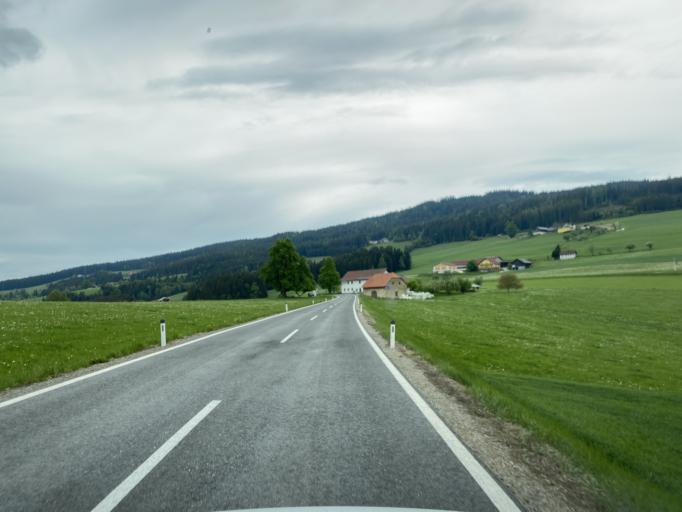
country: AT
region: Styria
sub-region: Politischer Bezirk Weiz
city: Gschaid bei Birkfeld
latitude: 47.3377
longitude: 15.7463
